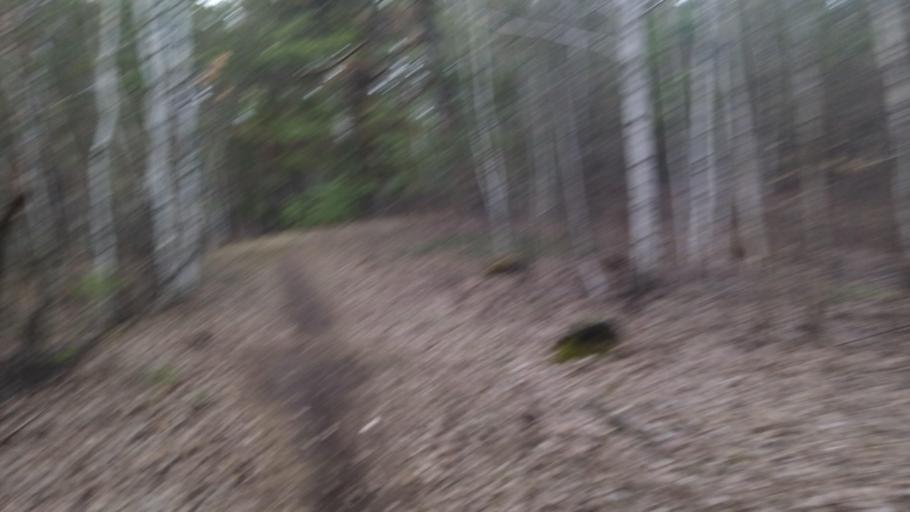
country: RU
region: Chelyabinsk
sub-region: Gorod Chelyabinsk
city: Chelyabinsk
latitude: 55.1398
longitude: 61.3400
